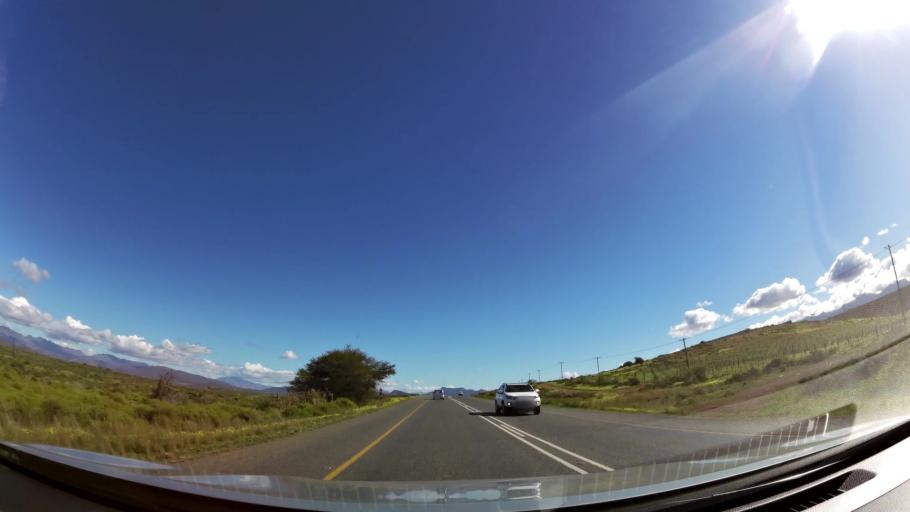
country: ZA
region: Western Cape
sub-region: Cape Winelands District Municipality
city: Ashton
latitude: -33.8177
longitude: 19.9525
